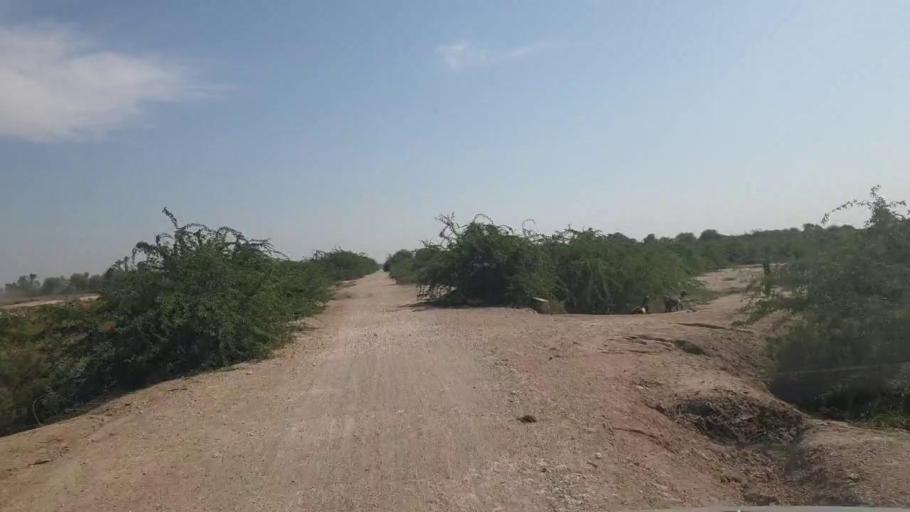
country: PK
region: Sindh
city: Digri
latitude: 24.9596
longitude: 69.1306
